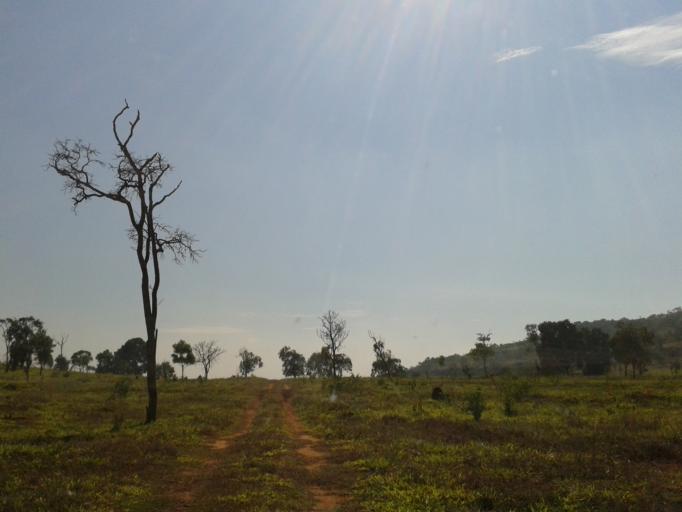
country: BR
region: Minas Gerais
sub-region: Campina Verde
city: Campina Verde
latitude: -19.3902
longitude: -49.6324
